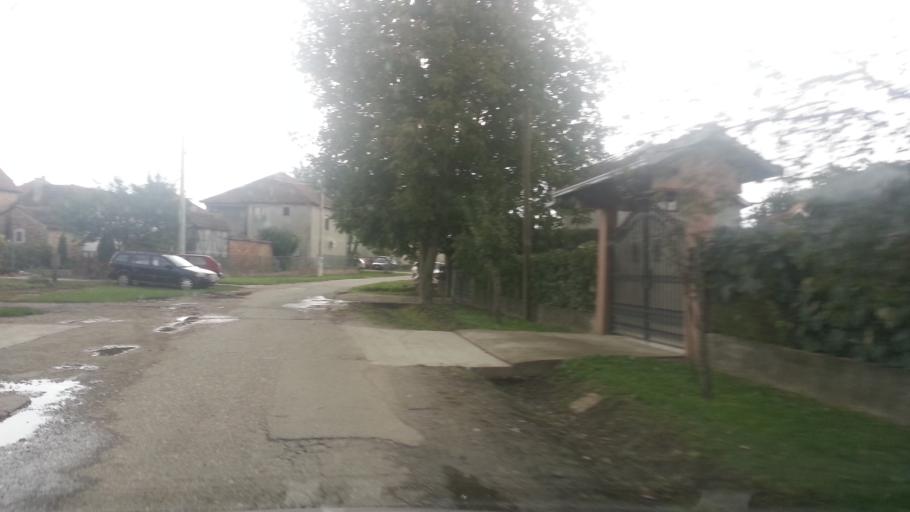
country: RS
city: Novi Banovci
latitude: 44.9603
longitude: 20.2763
